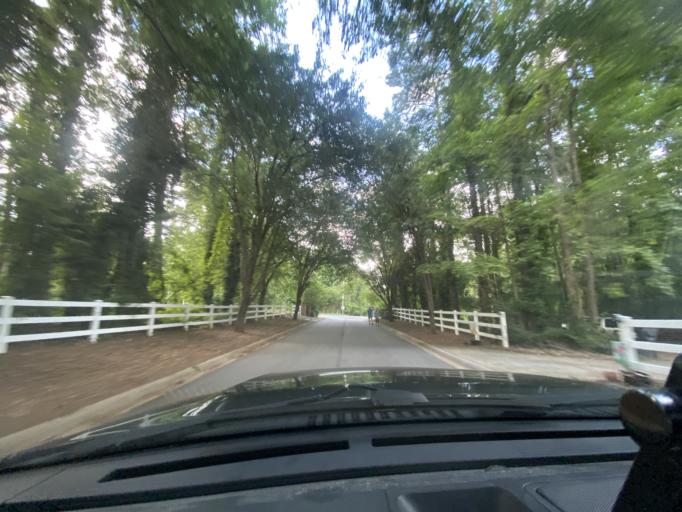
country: US
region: Georgia
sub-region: Fulton County
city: Palmetto
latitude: 33.4339
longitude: -84.6838
